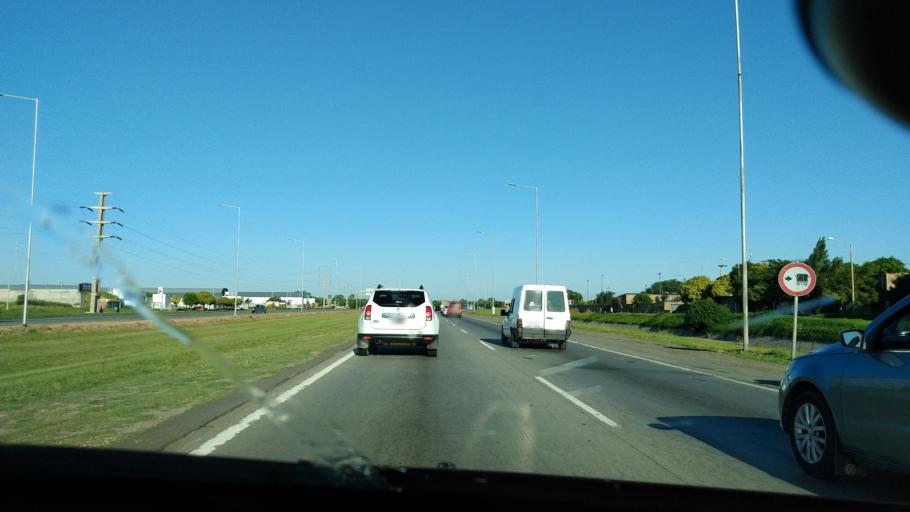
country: AR
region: Cordoba
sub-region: Departamento de Capital
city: Cordoba
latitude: -31.3636
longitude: -64.1395
